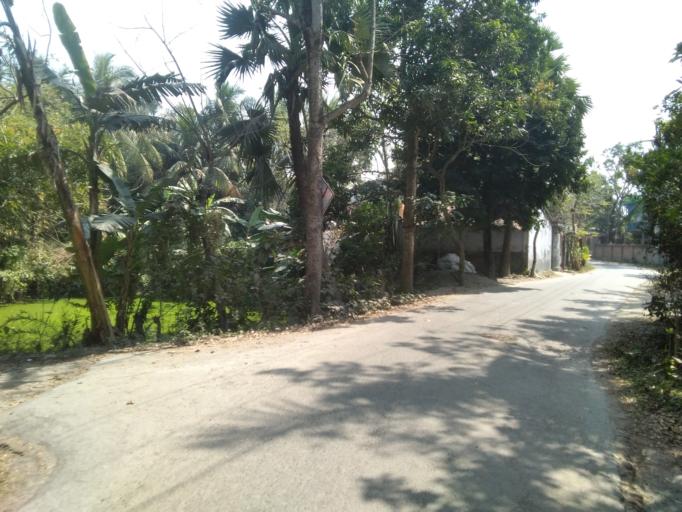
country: IN
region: West Bengal
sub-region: North 24 Parganas
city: Taki
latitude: 22.5915
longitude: 88.9953
